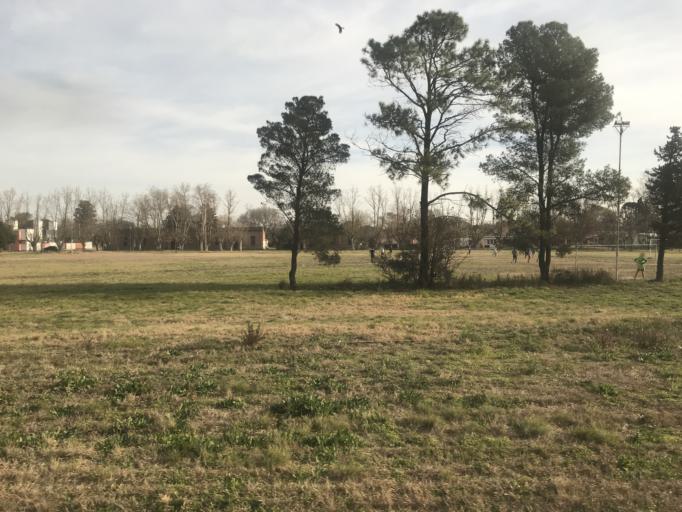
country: AR
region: Cordoba
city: Pilar
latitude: -31.6840
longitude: -63.8841
